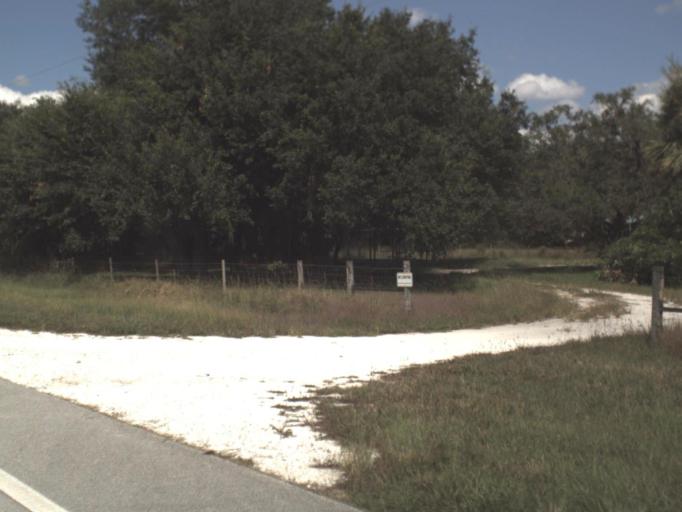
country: US
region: Florida
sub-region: Highlands County
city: Lake Placid
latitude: 27.4023
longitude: -81.1686
